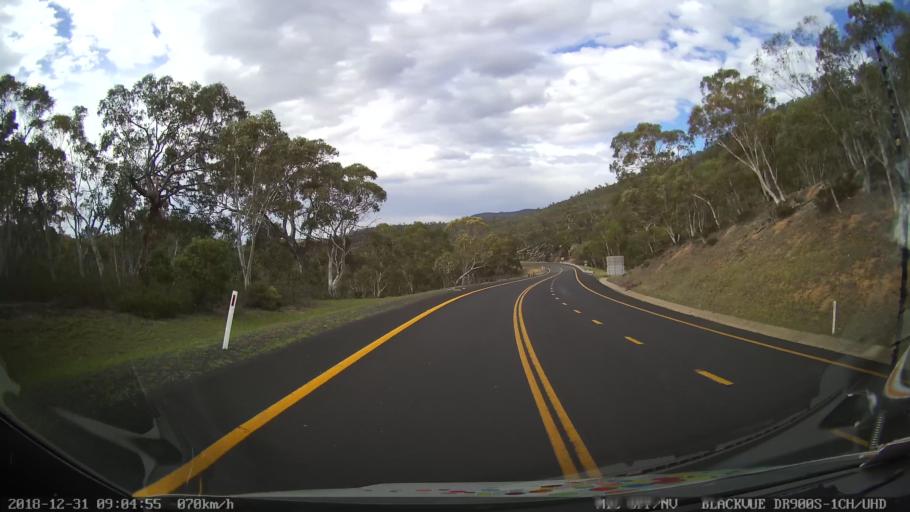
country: AU
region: New South Wales
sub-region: Snowy River
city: Jindabyne
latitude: -36.3582
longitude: 148.5895
